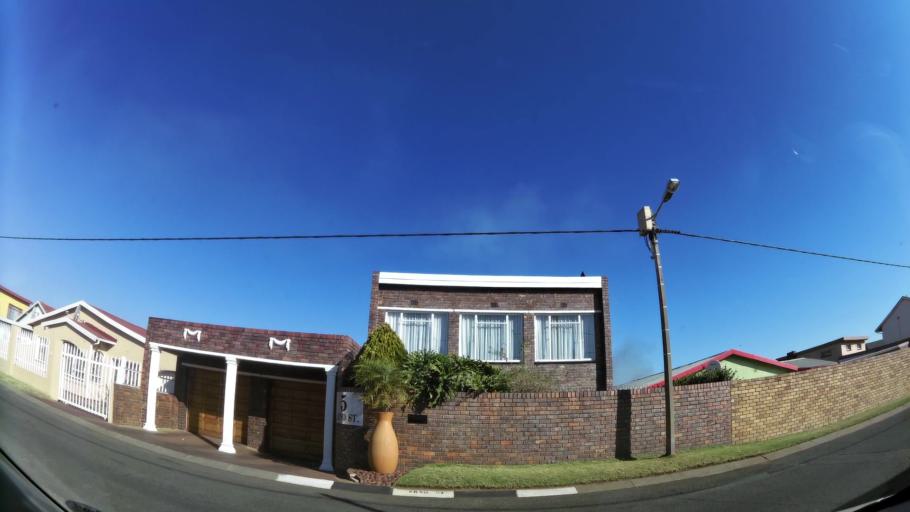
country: ZA
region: Gauteng
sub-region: City of Johannesburg Metropolitan Municipality
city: Johannesburg
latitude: -26.2097
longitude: 27.9748
